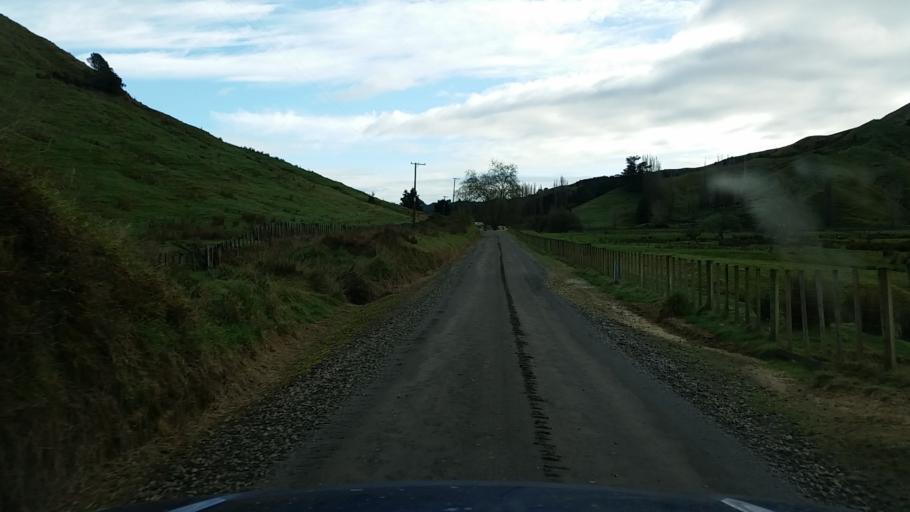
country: NZ
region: Taranaki
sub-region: New Plymouth District
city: Waitara
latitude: -39.0880
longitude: 174.8323
